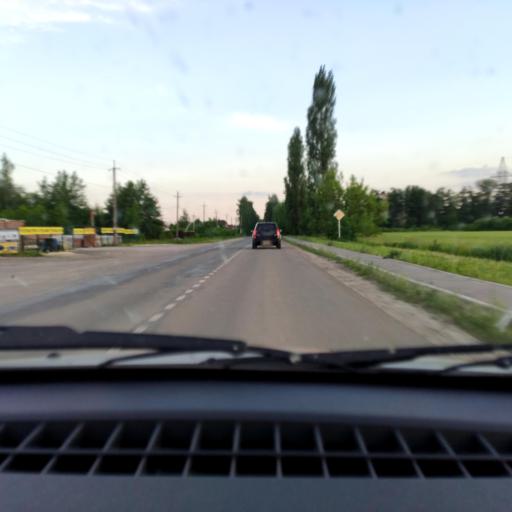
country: RU
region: Voronezj
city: Ramon'
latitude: 51.9437
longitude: 39.3525
